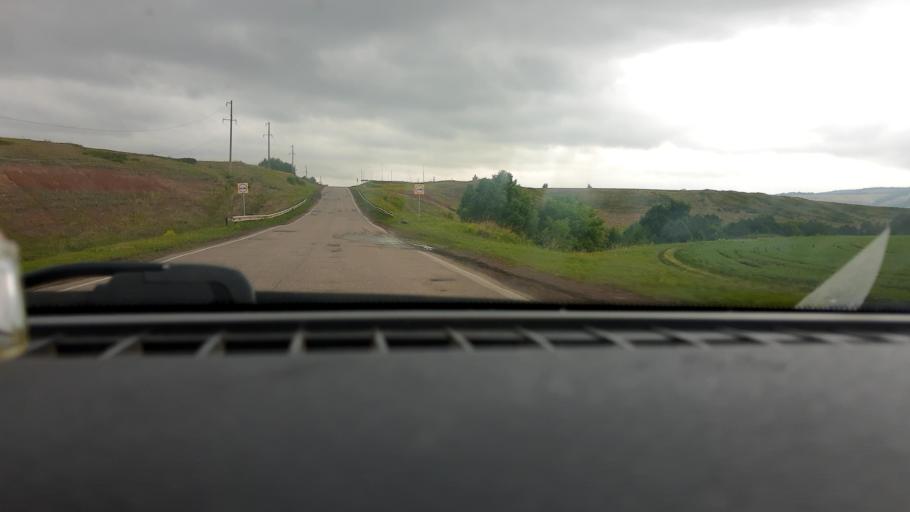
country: RU
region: Bashkortostan
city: Belebey
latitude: 54.3411
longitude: 54.0451
